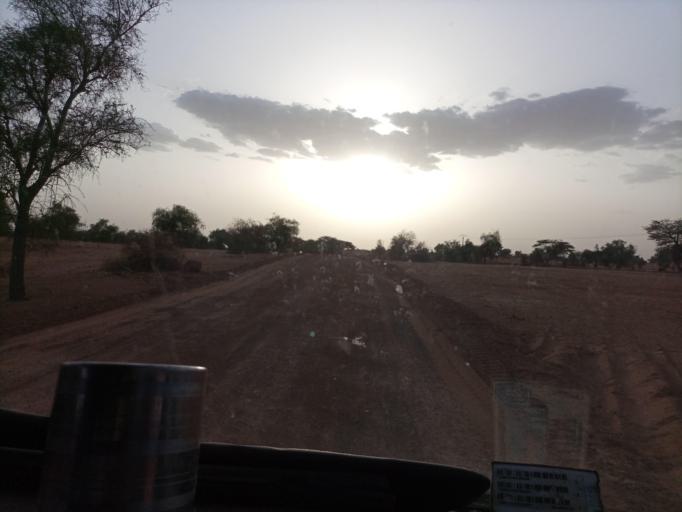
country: SN
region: Louga
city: Dara
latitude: 15.3773
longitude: -15.5935
